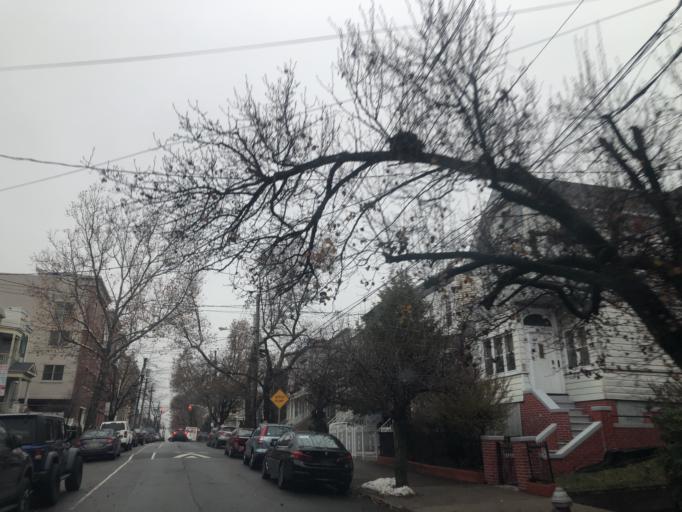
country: US
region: New Jersey
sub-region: Hudson County
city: Hoboken
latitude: 40.7471
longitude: -74.0501
